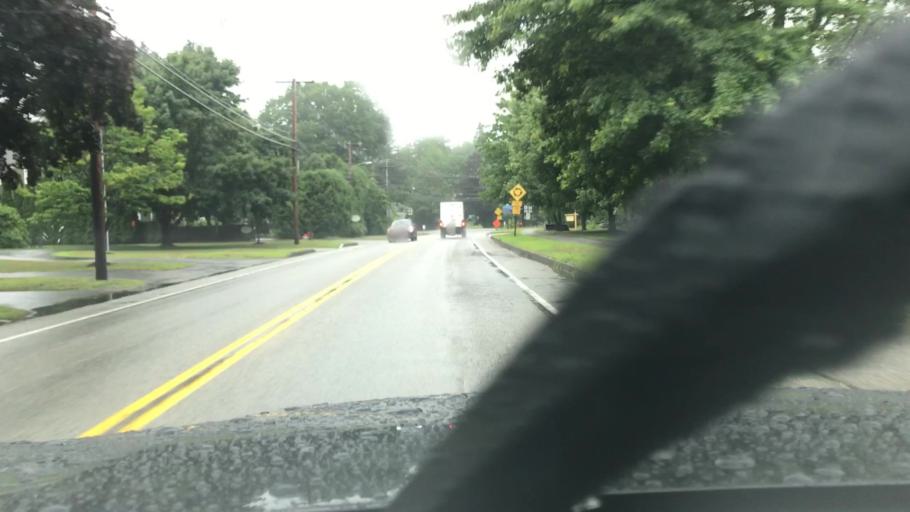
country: US
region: Maine
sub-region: York County
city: Kennebunk
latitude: 43.3918
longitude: -70.5465
